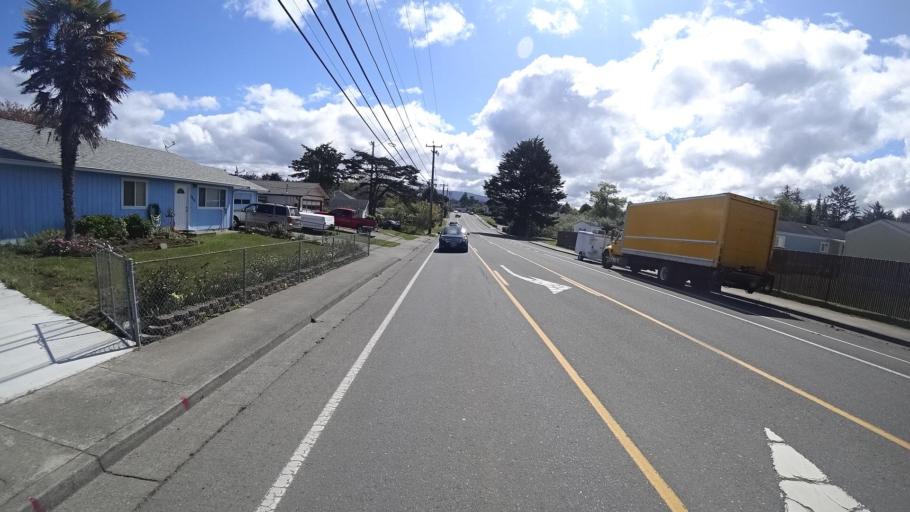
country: US
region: California
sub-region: Humboldt County
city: McKinleyville
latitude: 40.9360
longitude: -124.0962
